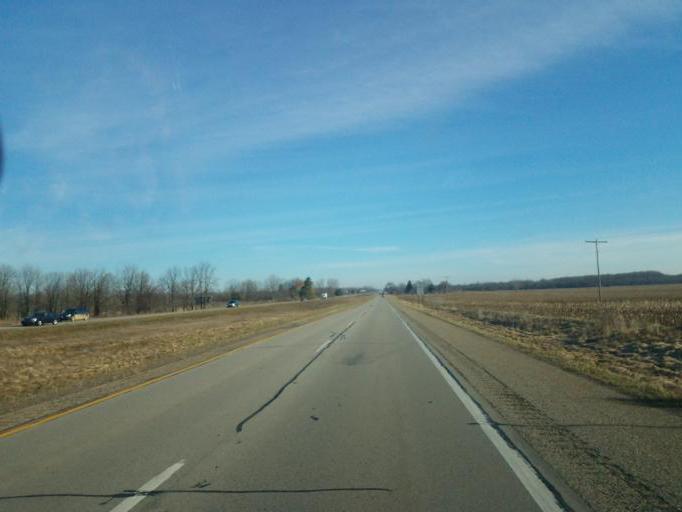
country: US
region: Michigan
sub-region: Clinton County
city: Saint Johns
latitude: 43.1197
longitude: -84.5631
